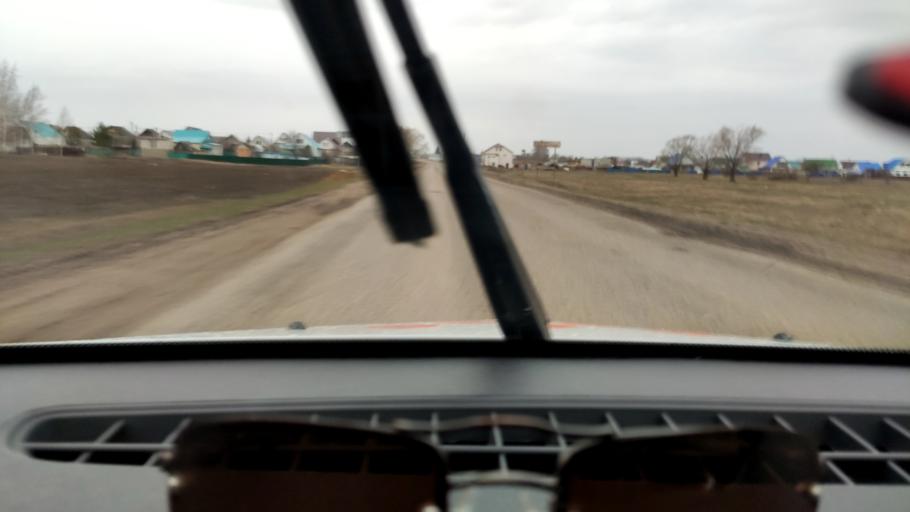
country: RU
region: Bashkortostan
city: Kabakovo
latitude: 54.5481
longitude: 56.1023
